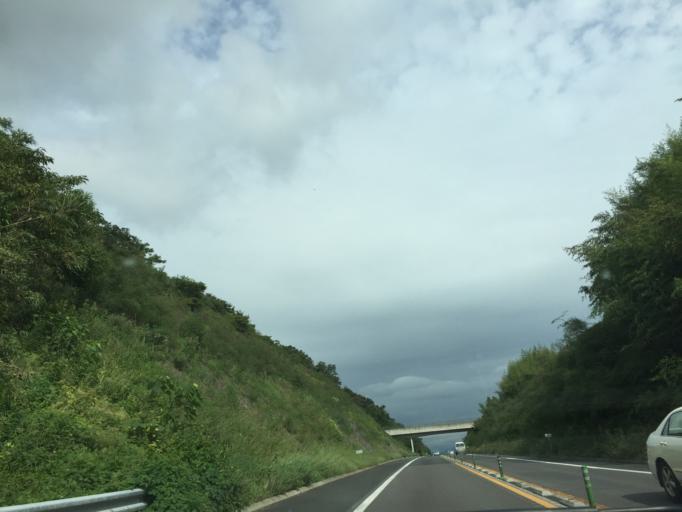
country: JP
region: Kagawa
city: Shido
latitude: 34.2633
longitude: 134.2871
